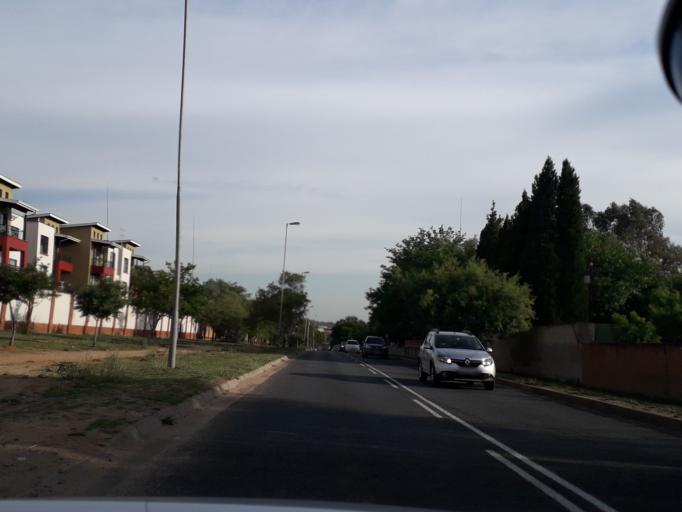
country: ZA
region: Gauteng
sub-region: City of Johannesburg Metropolitan Municipality
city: Diepsloot
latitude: -26.0318
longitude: 27.9921
